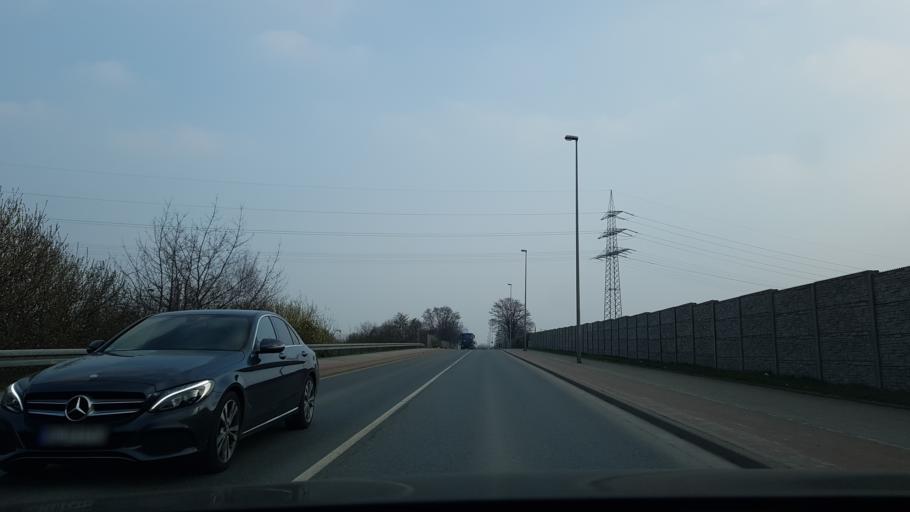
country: DE
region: North Rhine-Westphalia
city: Meiderich
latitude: 51.5239
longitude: 6.8102
